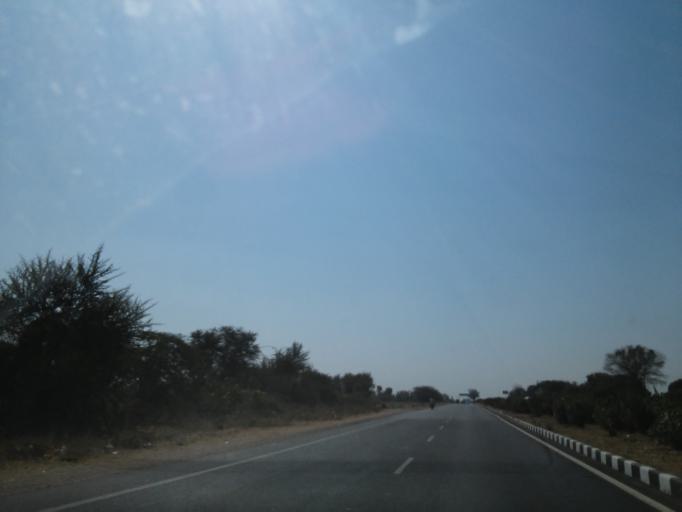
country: IN
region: Gujarat
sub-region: Gandhinagar
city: Chhala
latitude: 23.4277
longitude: 72.8416
